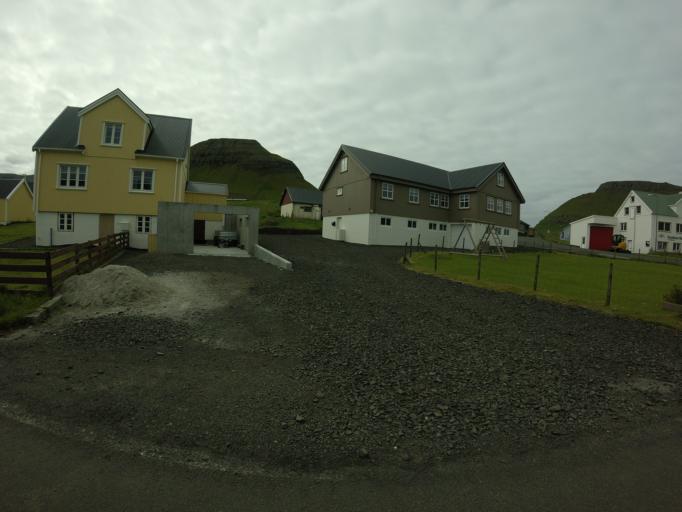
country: FO
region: Suduroy
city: Tvoroyri
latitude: 61.5981
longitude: -6.9515
